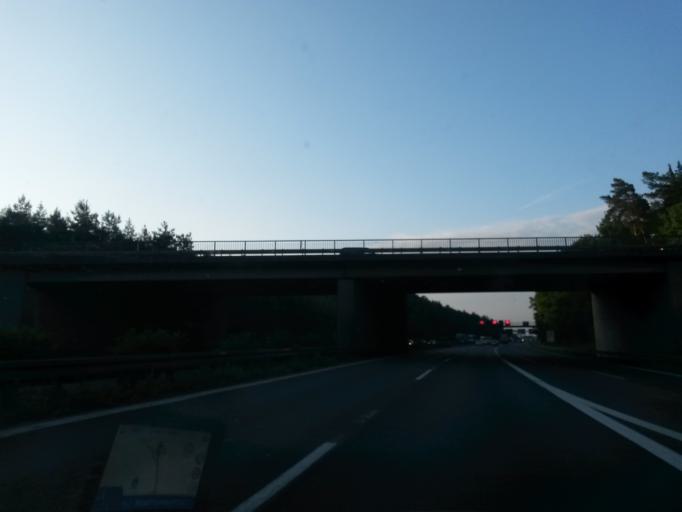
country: DE
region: Bavaria
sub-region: Regierungsbezirk Mittelfranken
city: Wendelstein
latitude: 49.3922
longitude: 11.1157
